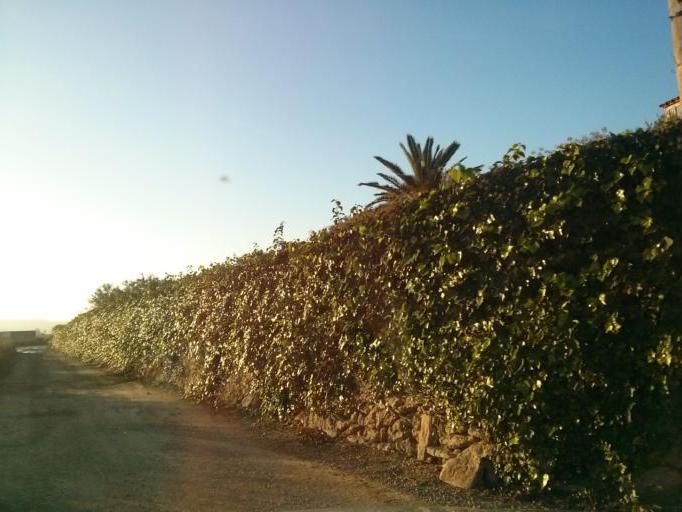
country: ES
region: Catalonia
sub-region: Provincia de Tarragona
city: Santa Oliva
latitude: 41.2493
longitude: 1.5424
